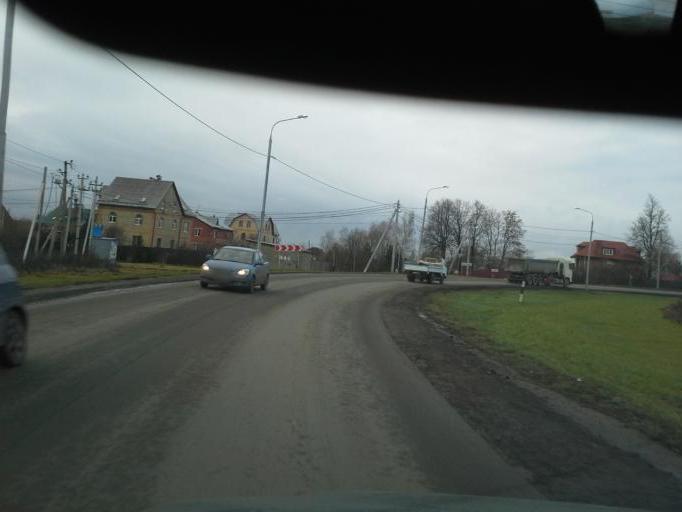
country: RU
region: Moskovskaya
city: Kommunarka
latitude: 55.5585
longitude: 37.4204
